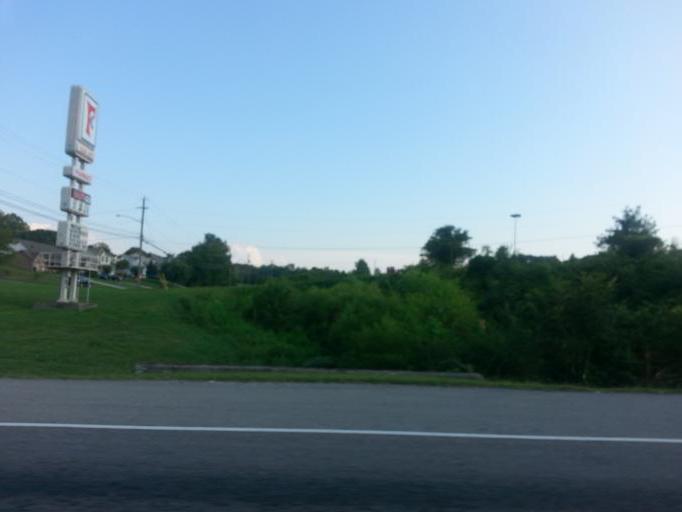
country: US
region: Tennessee
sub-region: Knox County
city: Mascot
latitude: 36.0214
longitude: -83.7770
